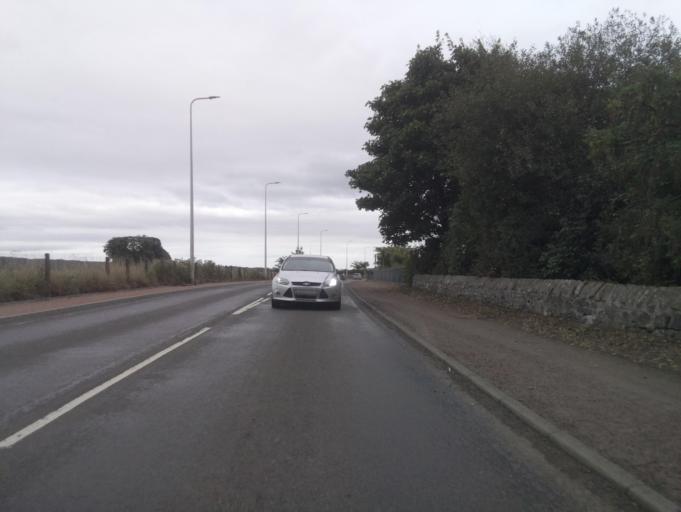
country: GB
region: Scotland
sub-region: Fife
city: Leslie
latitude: 56.2016
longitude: -3.2275
